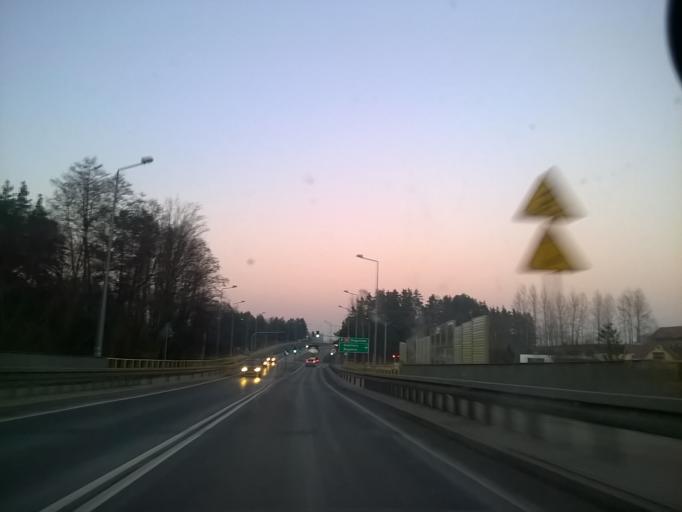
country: PL
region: Warmian-Masurian Voivodeship
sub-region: Powiat olsztynski
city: Barczewo
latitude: 53.8027
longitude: 20.6210
